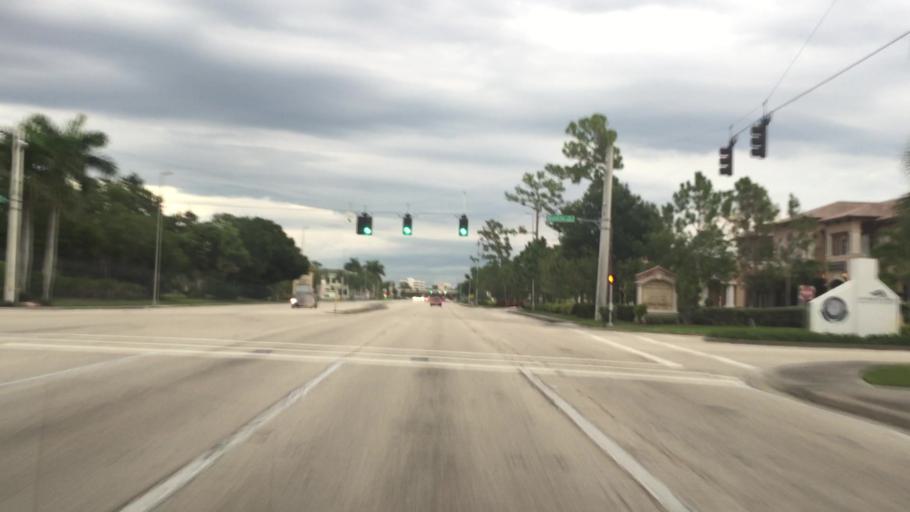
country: US
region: Florida
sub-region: Lee County
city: Whiskey Creek
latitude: 26.5568
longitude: -81.8939
